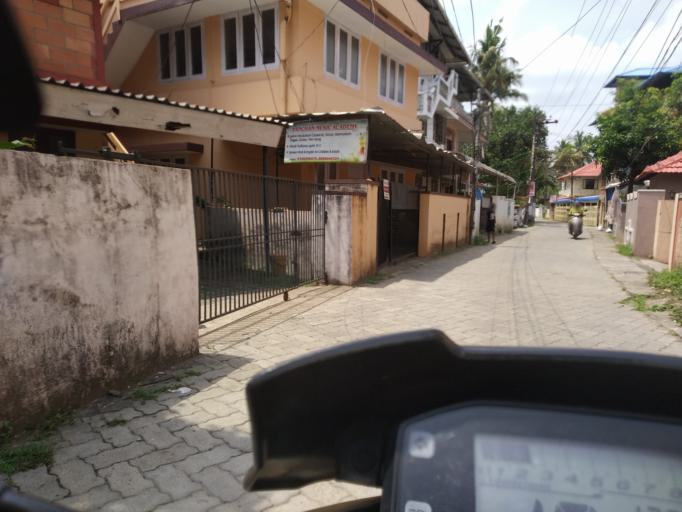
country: IN
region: Kerala
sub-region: Ernakulam
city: Elur
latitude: 10.0161
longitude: 76.3264
